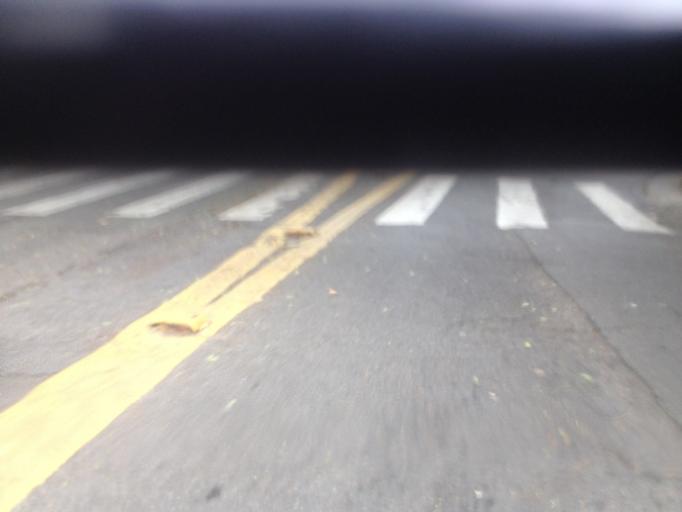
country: BR
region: Sao Paulo
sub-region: Sao Paulo
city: Sao Paulo
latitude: -23.5683
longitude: -46.6807
